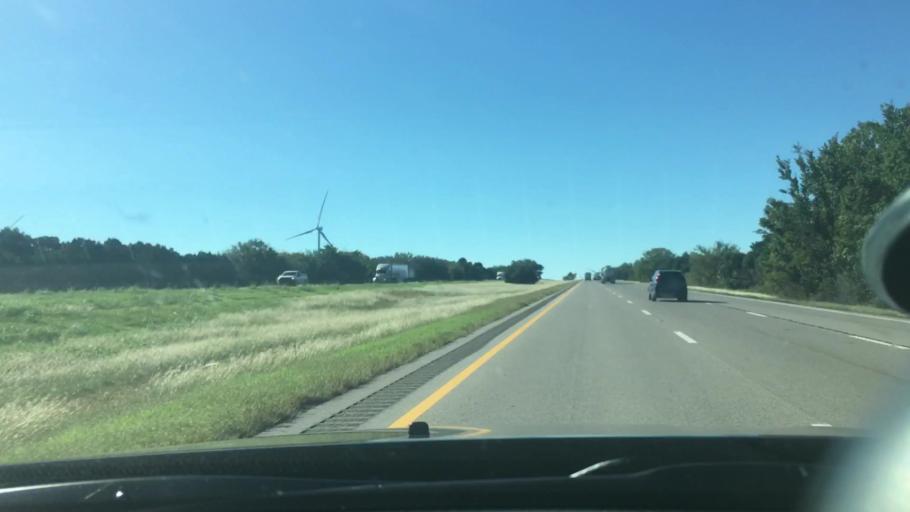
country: US
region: Oklahoma
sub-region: Murray County
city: Davis
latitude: 34.4124
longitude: -97.1387
